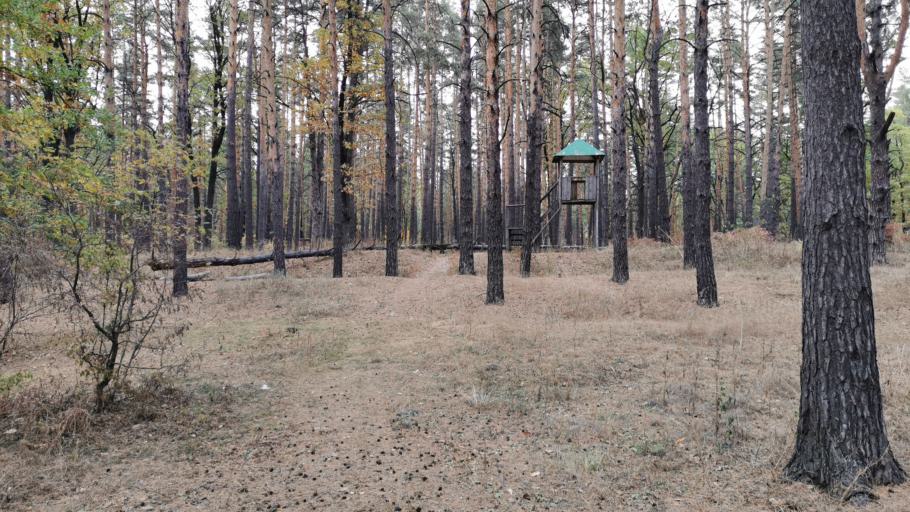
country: RU
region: Lipetsk
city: Kazinka
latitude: 52.5955
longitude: 39.7673
